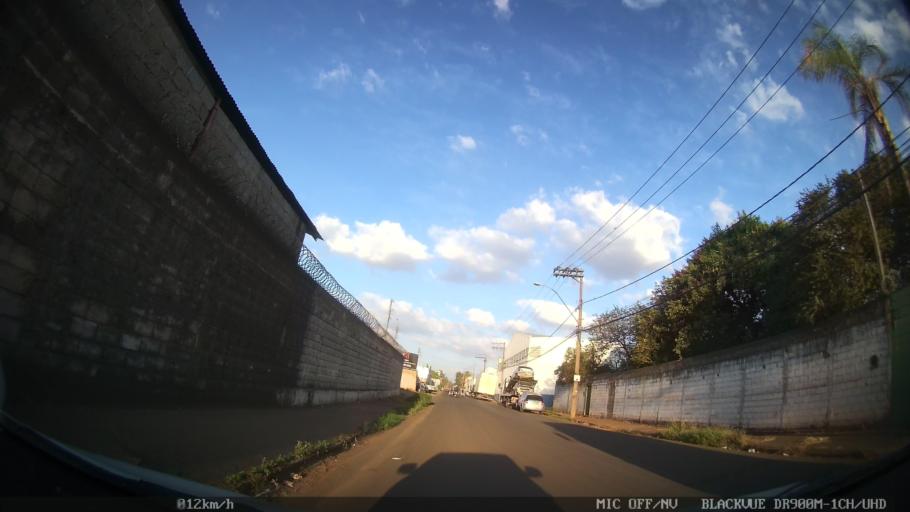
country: BR
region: Sao Paulo
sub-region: Ribeirao Preto
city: Ribeirao Preto
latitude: -21.1435
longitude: -47.7877
